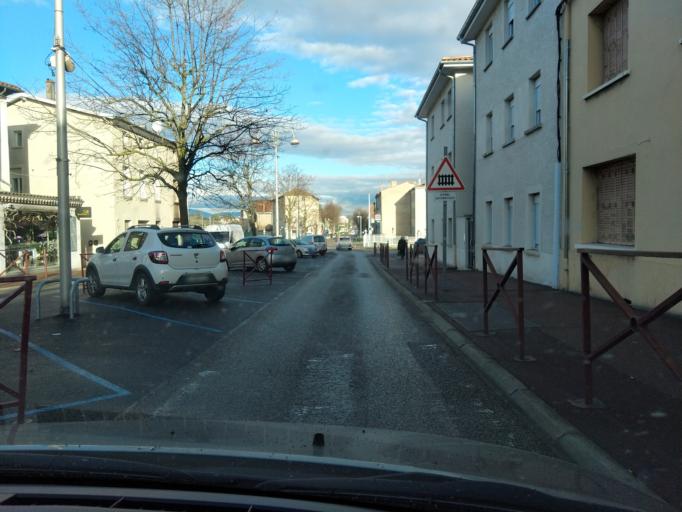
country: FR
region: Rhone-Alpes
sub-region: Departement de l'Isere
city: Chanas
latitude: 45.2944
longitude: 4.8130
